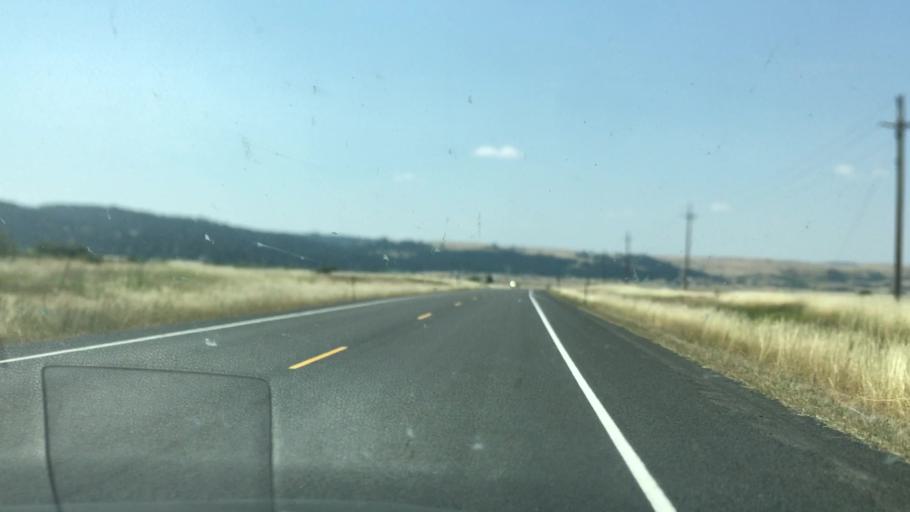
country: US
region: Idaho
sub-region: Idaho County
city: Grangeville
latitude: 45.8965
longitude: -116.1851
